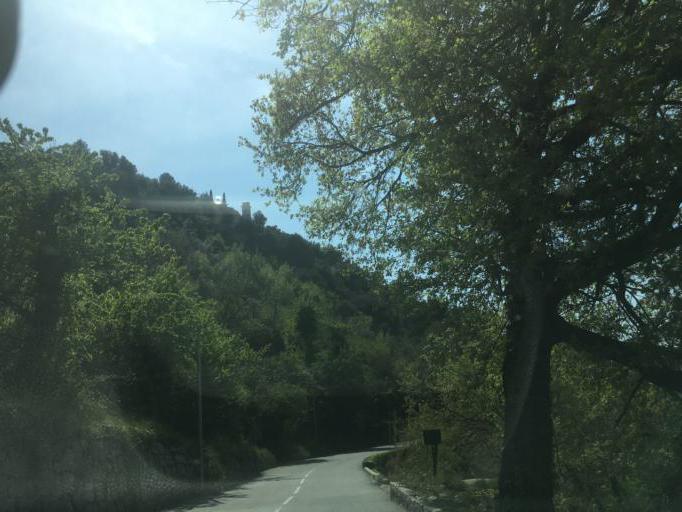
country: FR
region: Provence-Alpes-Cote d'Azur
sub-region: Departement des Alpes-Maritimes
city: Saint-Martin-du-Var
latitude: 43.8302
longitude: 7.1994
